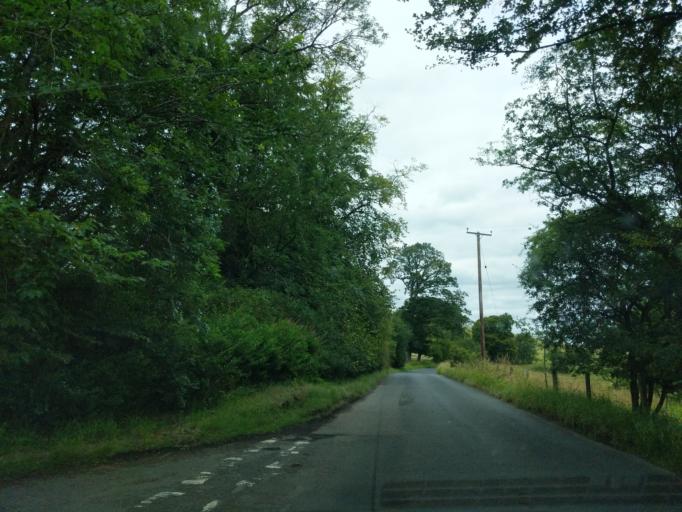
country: GB
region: Scotland
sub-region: The Scottish Borders
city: West Linton
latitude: 55.6995
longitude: -3.3380
